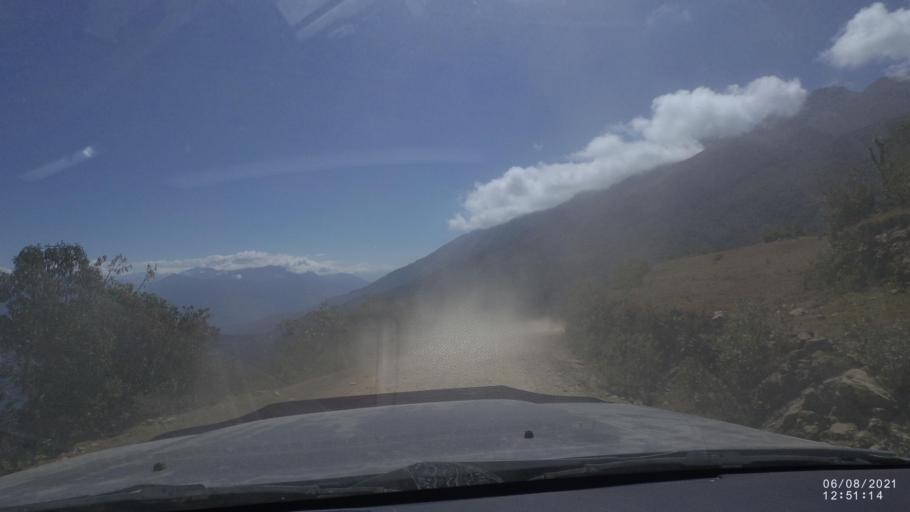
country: BO
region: Cochabamba
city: Colchani
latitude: -16.7604
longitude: -66.6793
